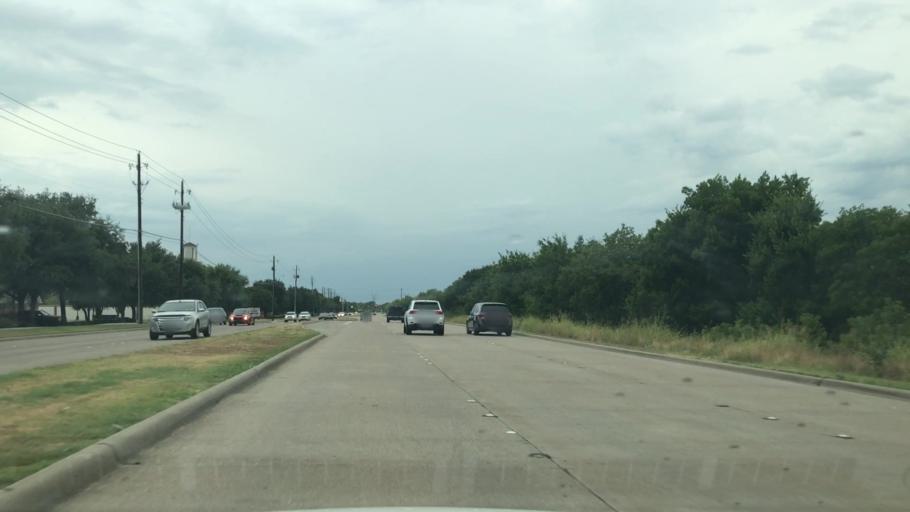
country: US
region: Texas
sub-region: Dallas County
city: Farmers Branch
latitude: 32.9523
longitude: -96.9510
